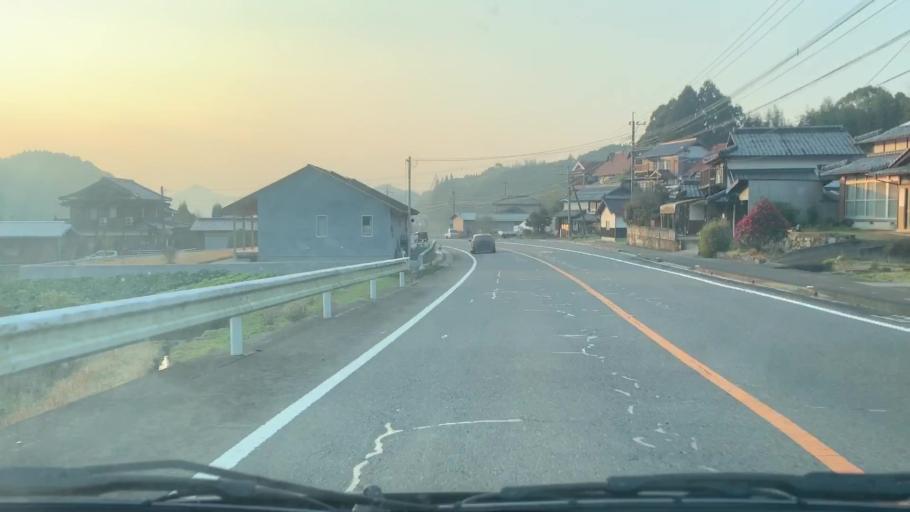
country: JP
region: Saga Prefecture
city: Takeocho-takeo
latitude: 33.2559
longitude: 130.0104
